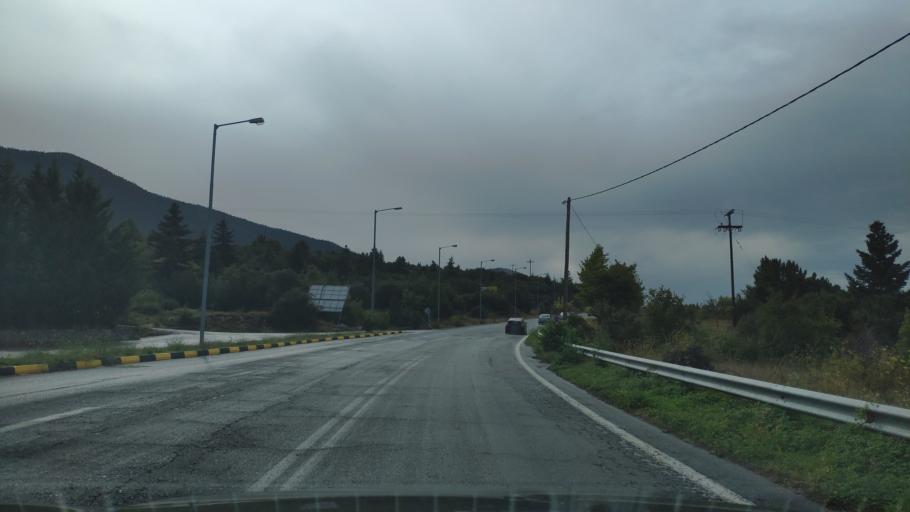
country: GR
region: Peloponnese
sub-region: Nomos Arkadias
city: Langadhia
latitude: 37.6807
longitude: 22.1917
